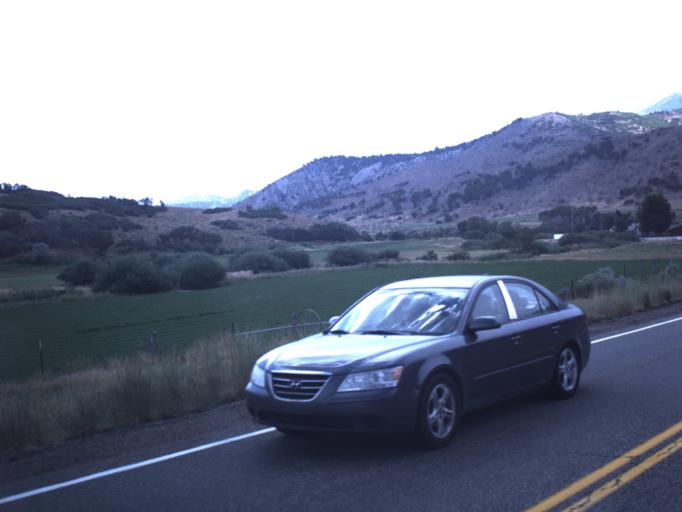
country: US
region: Utah
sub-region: Juab County
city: Nephi
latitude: 39.7157
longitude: -111.7252
